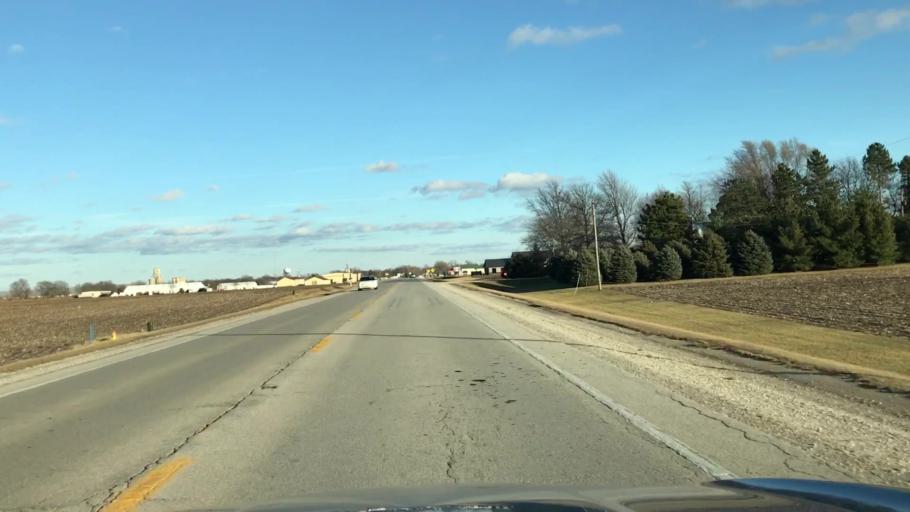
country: US
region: Illinois
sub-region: Livingston County
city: Fairbury
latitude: 40.7439
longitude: -88.5427
